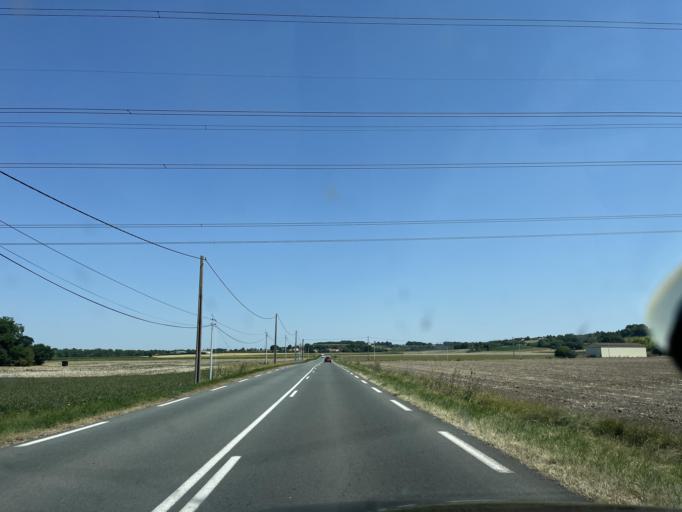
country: FR
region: Poitou-Charentes
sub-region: Departement de la Charente-Maritime
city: Mirambeau
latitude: 45.4182
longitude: -0.6298
